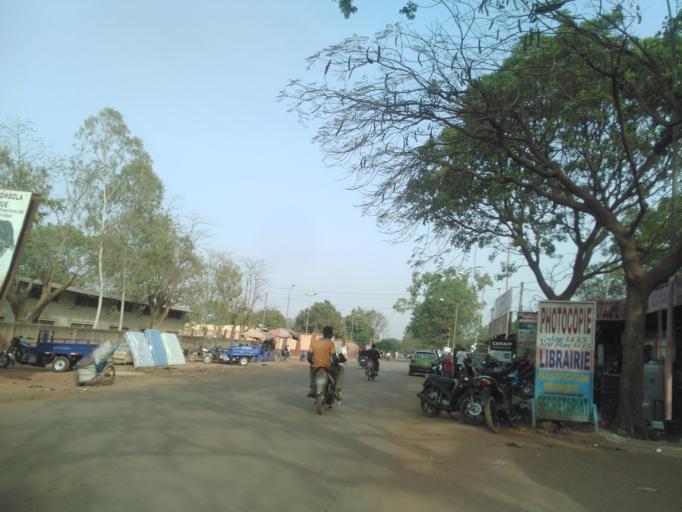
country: BF
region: High-Basins
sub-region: Province du Houet
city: Bobo-Dioulasso
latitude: 11.1740
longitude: -4.3071
